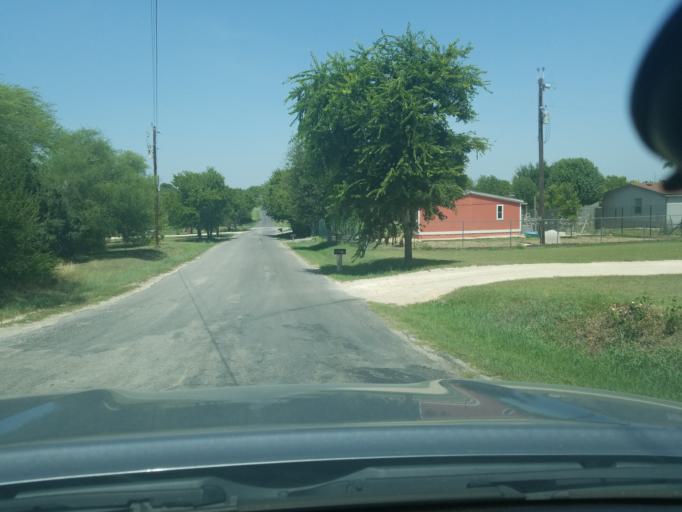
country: US
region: Texas
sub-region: Guadalupe County
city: Cibolo
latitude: 29.5860
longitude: -98.2035
